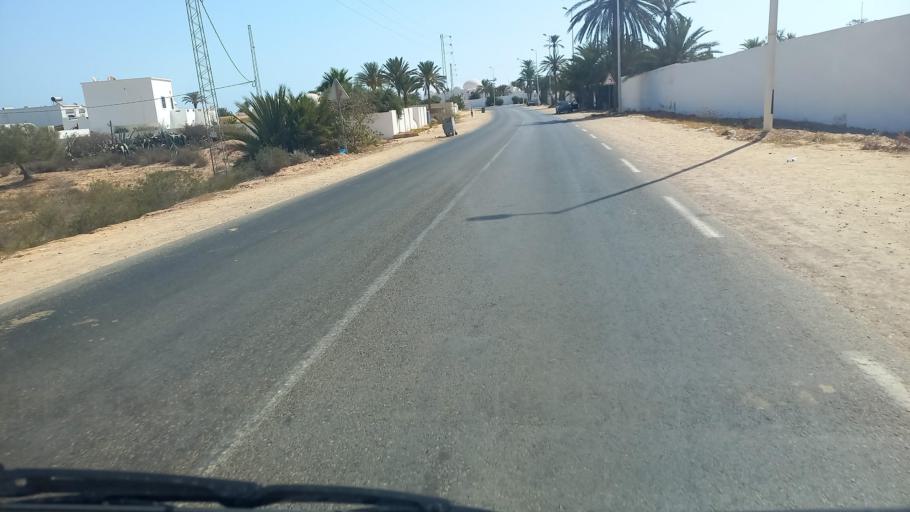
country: TN
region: Madanin
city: Midoun
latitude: 33.7820
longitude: 11.0523
